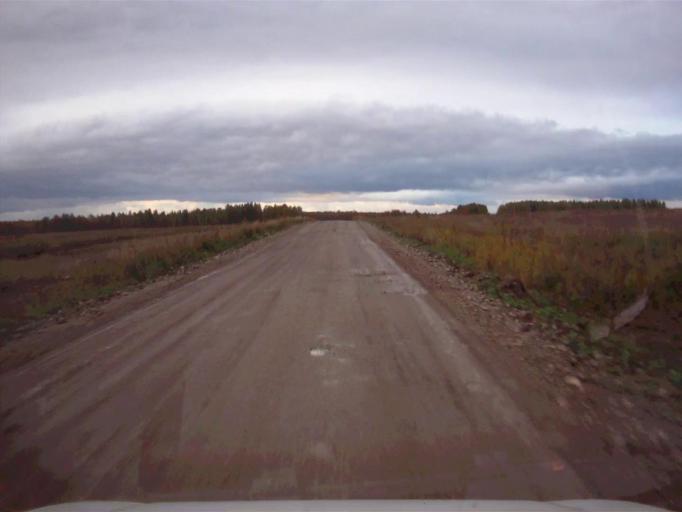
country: RU
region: Sverdlovsk
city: Mikhaylovsk
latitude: 56.1861
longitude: 59.1864
